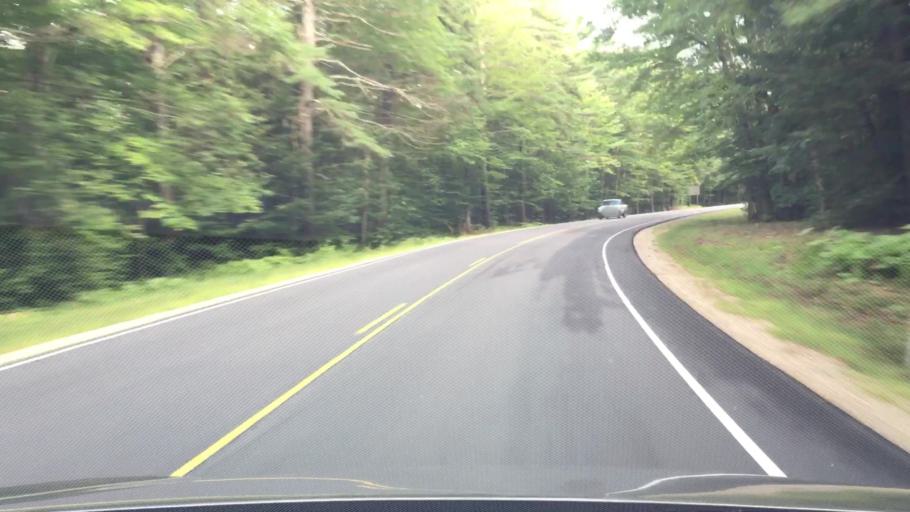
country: US
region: New Hampshire
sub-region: Carroll County
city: Conway
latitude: 43.9851
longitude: -71.1424
